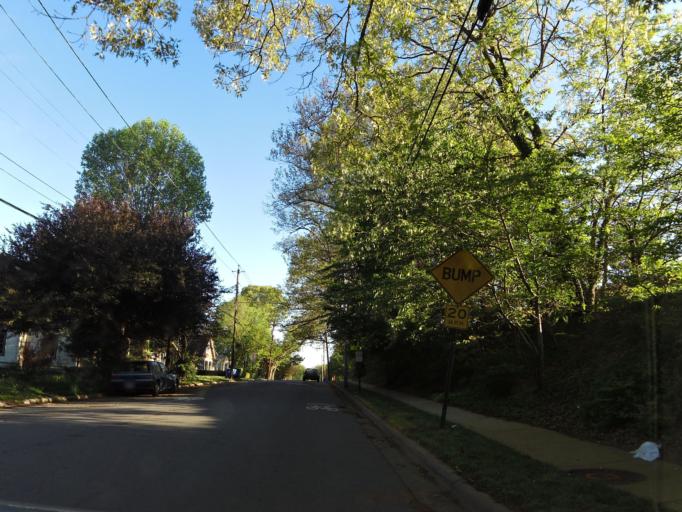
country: US
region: North Carolina
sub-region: Buncombe County
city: Asheville
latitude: 35.5877
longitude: -82.5594
